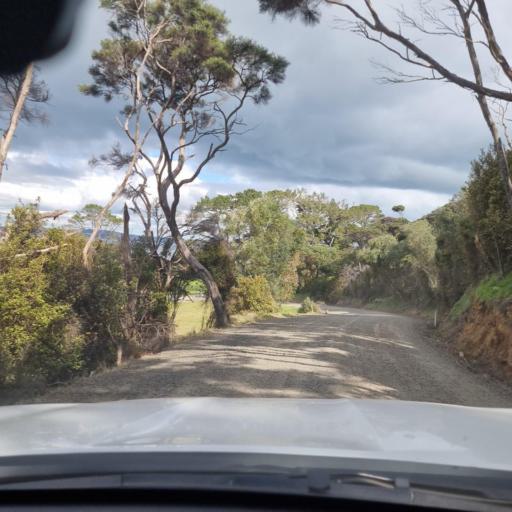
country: NZ
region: Auckland
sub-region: Auckland
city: Wellsford
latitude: -36.3617
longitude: 174.1778
